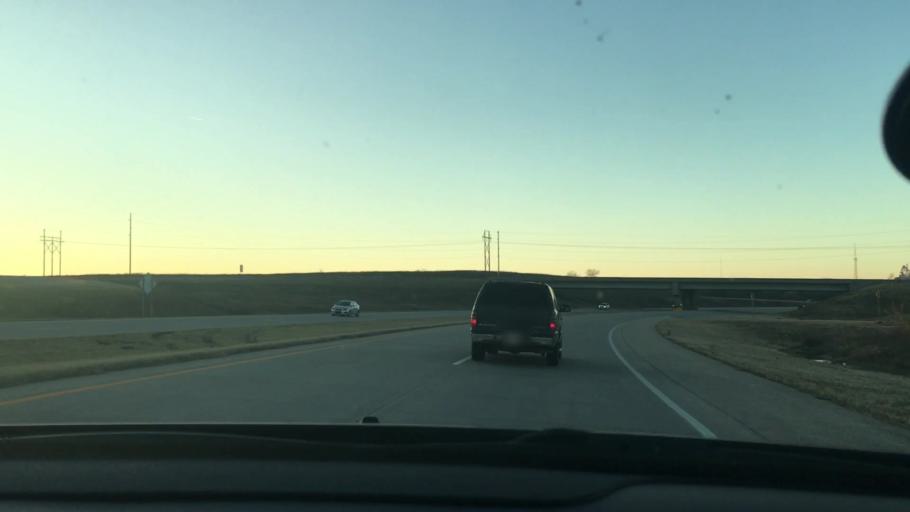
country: US
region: Oklahoma
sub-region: Pontotoc County
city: Ada
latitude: 34.7916
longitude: -96.6934
